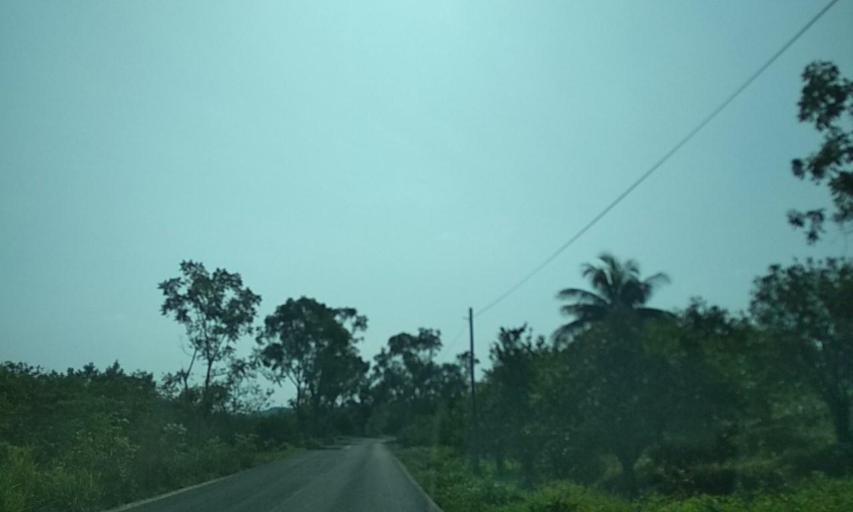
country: MX
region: Veracruz
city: Gutierrez Zamora
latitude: 20.3489
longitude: -97.1496
